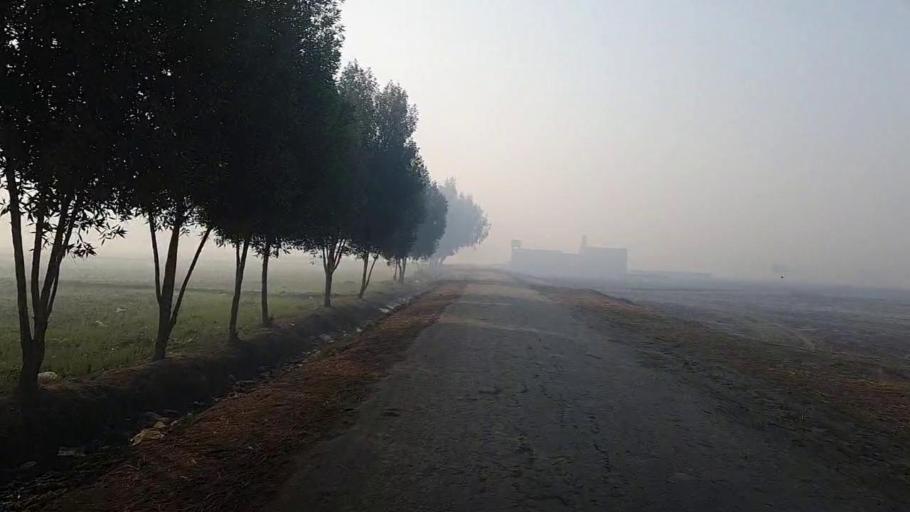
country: PK
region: Sindh
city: Mehar
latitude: 27.1684
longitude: 67.8235
